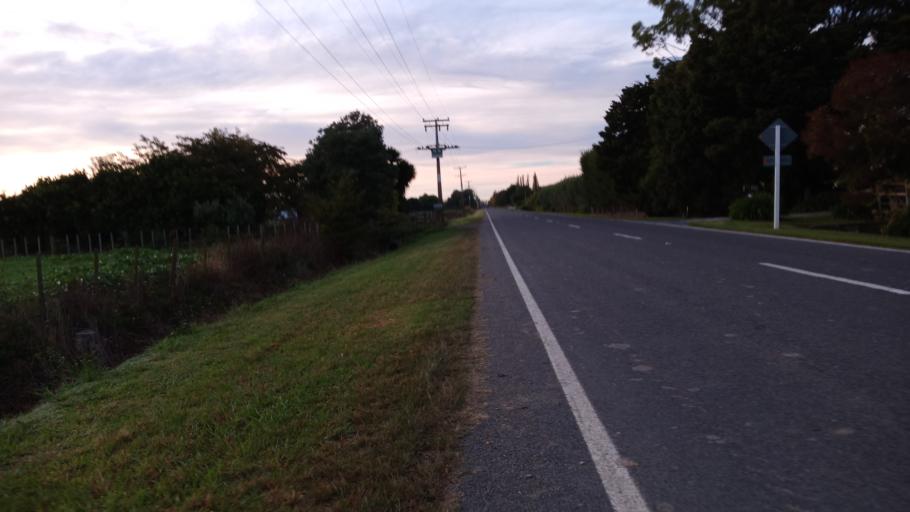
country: NZ
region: Gisborne
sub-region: Gisborne District
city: Gisborne
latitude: -38.6422
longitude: 177.9378
